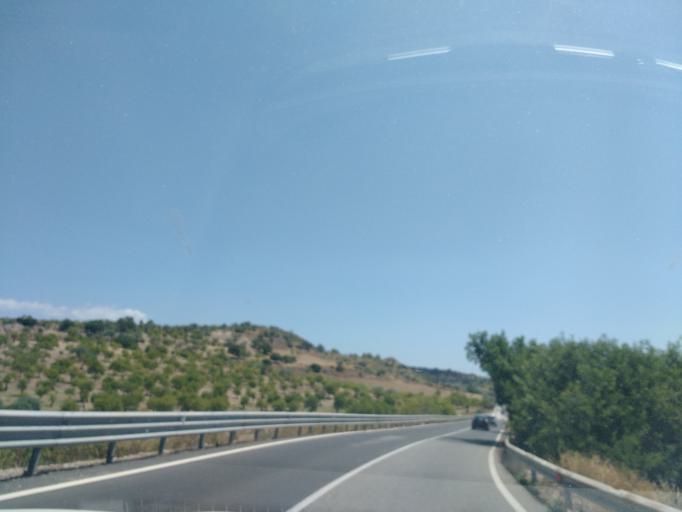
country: IT
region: Sicily
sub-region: Provincia di Siracusa
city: Noto
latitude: 36.8677
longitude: 15.0262
